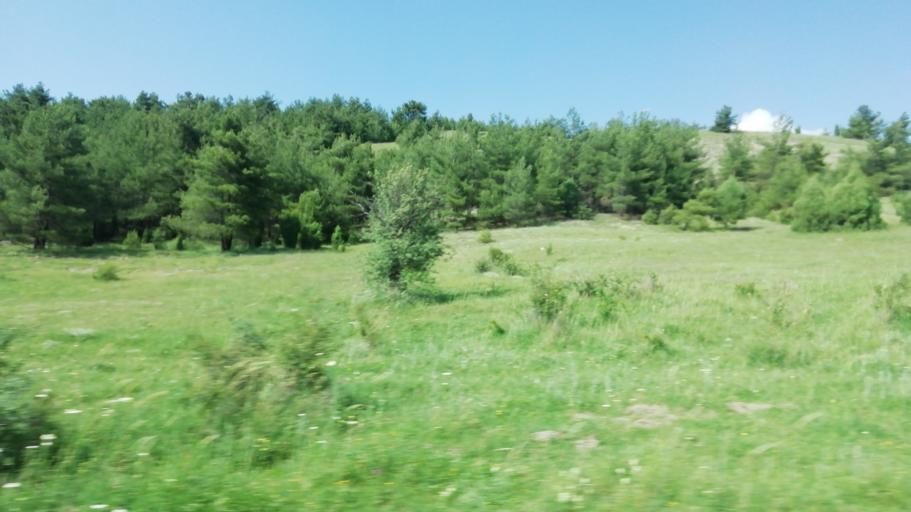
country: TR
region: Karabuk
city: Karabuk
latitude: 41.1313
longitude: 32.5666
